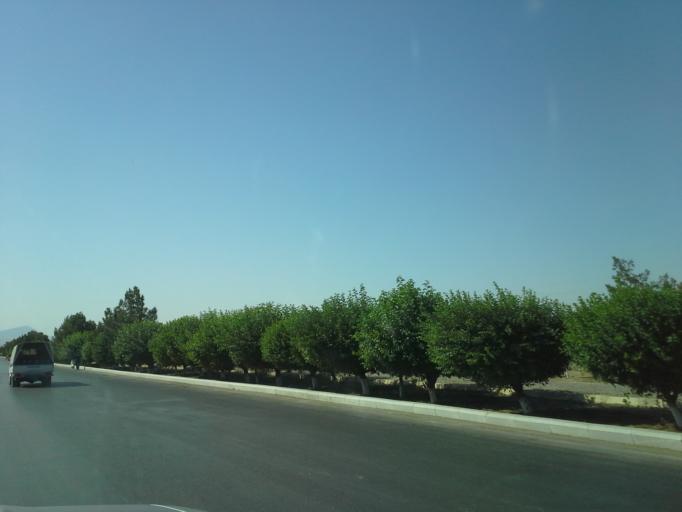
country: TM
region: Ahal
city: Annau
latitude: 37.9174
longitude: 58.4640
